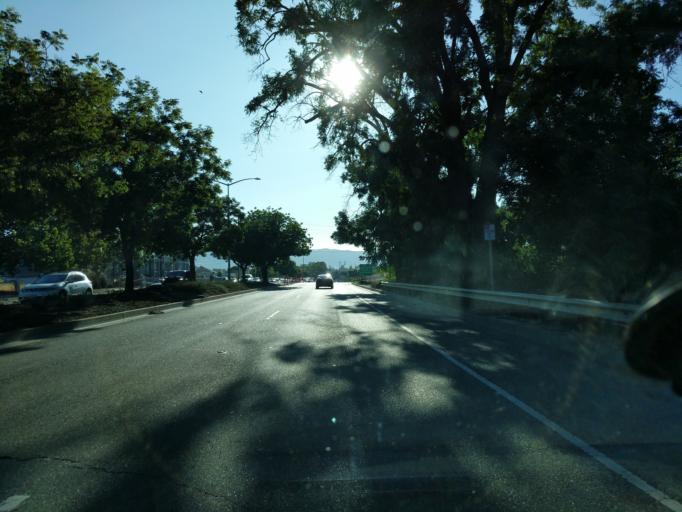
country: US
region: California
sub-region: Alameda County
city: Pleasanton
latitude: 37.6709
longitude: -121.8546
